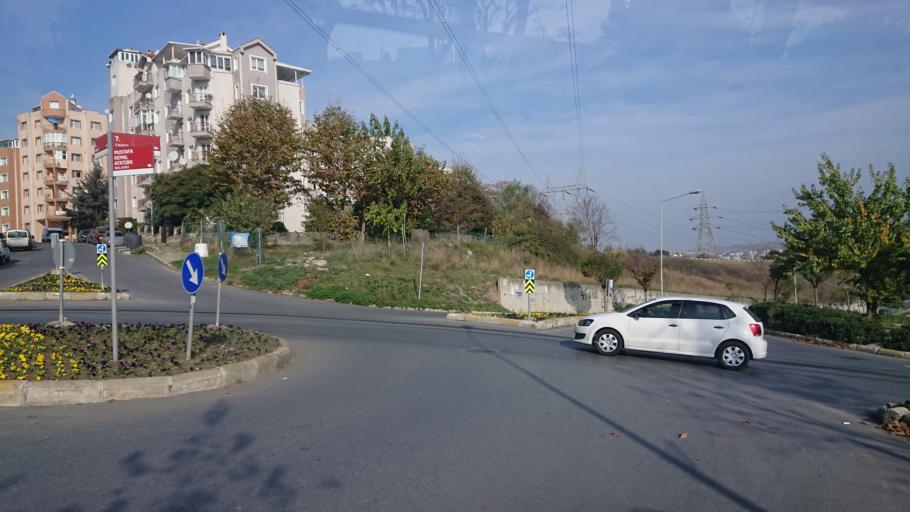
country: TR
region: Istanbul
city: Esenyurt
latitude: 41.0756
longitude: 28.6691
